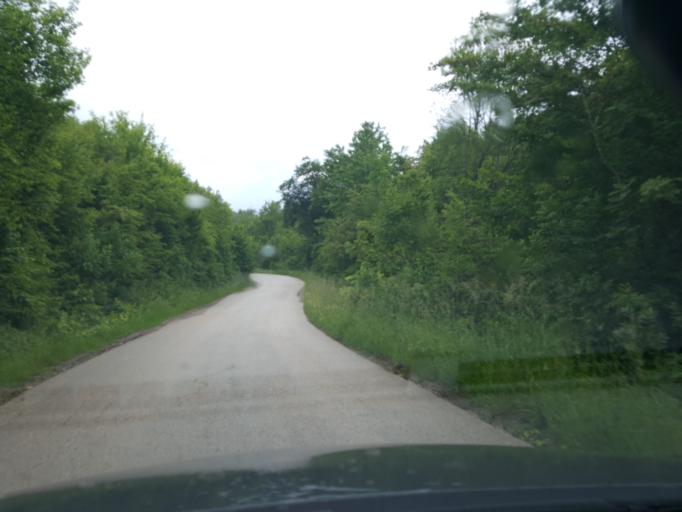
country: RS
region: Central Serbia
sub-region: Zajecarski Okrug
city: Boljevac
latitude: 43.7890
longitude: 21.9126
